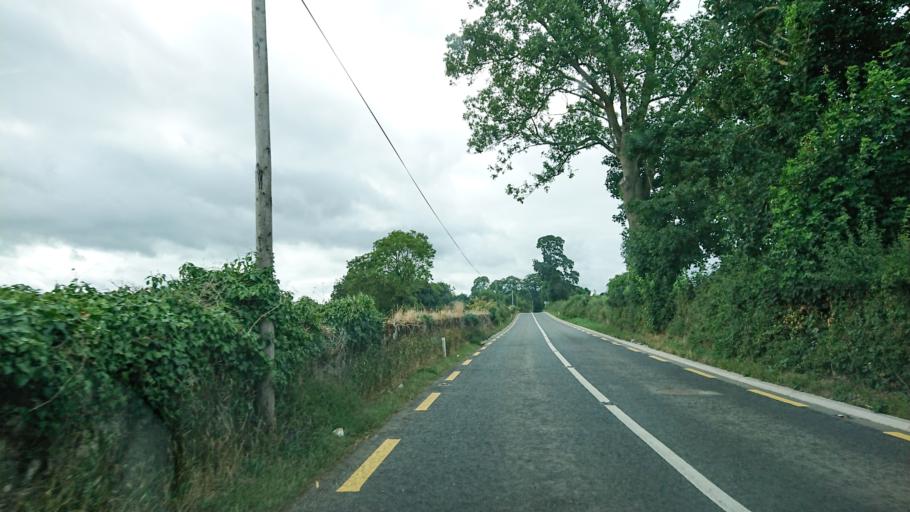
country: IE
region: Munster
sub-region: County Cork
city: Mallow
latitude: 52.1543
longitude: -8.5663
